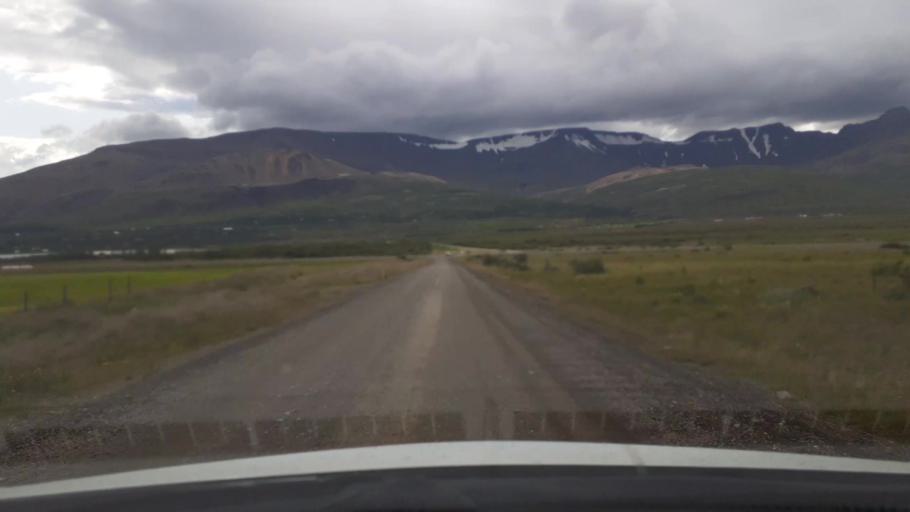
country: IS
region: West
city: Borgarnes
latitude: 64.5456
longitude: -21.6195
